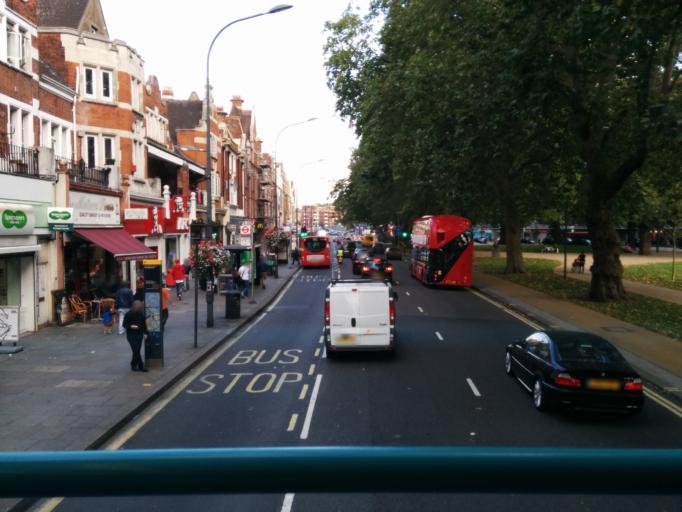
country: GB
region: England
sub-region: Greater London
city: Hammersmith
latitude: 51.5047
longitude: -0.2216
